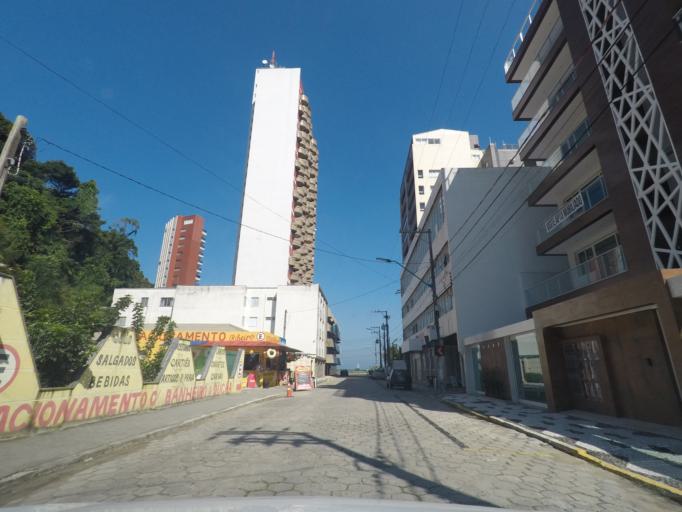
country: BR
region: Parana
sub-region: Guaratuba
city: Guaratuba
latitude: -25.8463
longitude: -48.5387
